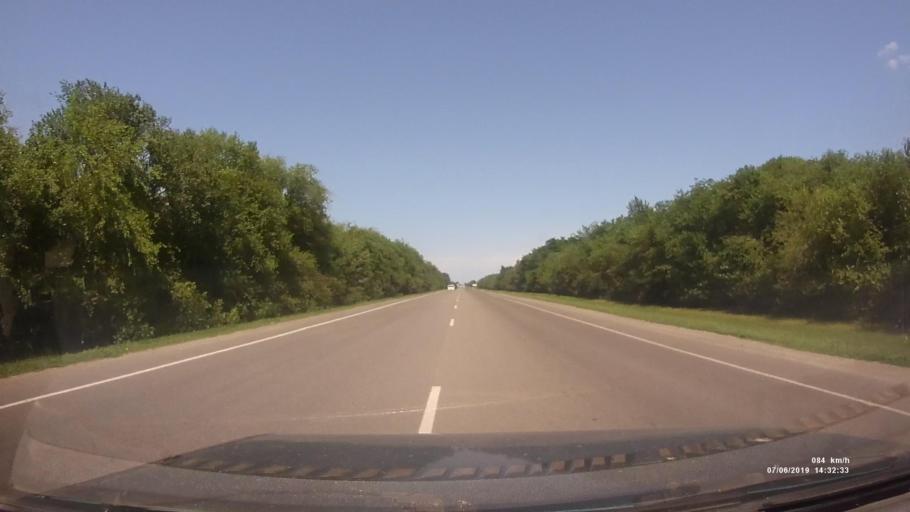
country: RU
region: Rostov
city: Kuleshovka
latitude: 47.0954
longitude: 39.6212
